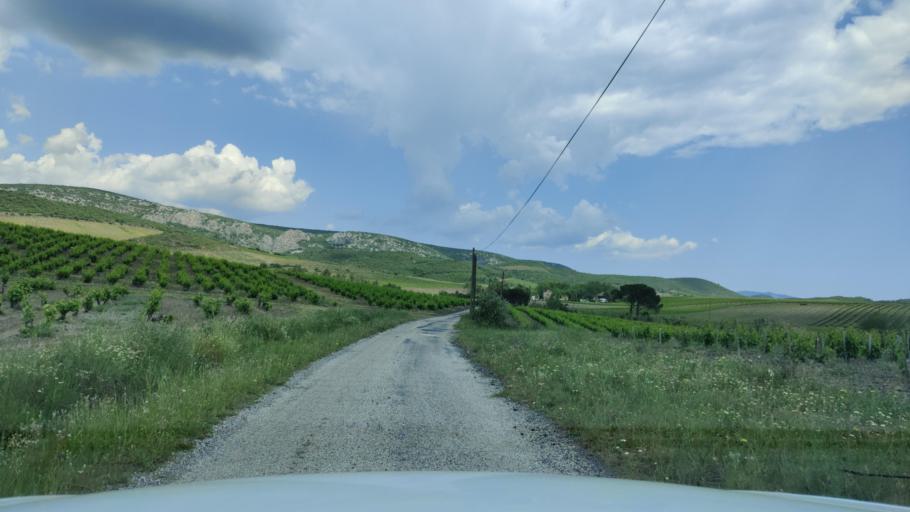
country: FR
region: Languedoc-Roussillon
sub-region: Departement des Pyrenees-Orientales
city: Estagel
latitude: 42.8151
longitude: 2.6801
